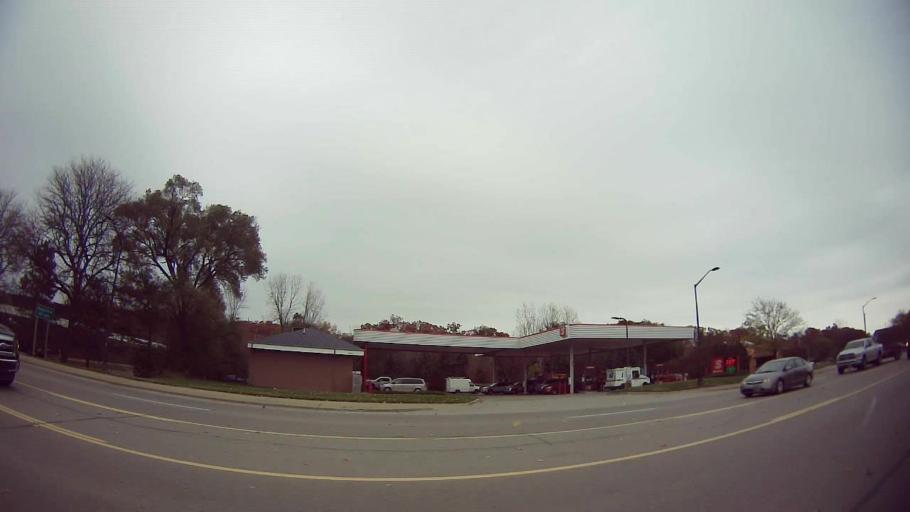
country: US
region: Michigan
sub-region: Oakland County
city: Clarkston
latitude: 42.7167
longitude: -83.4142
